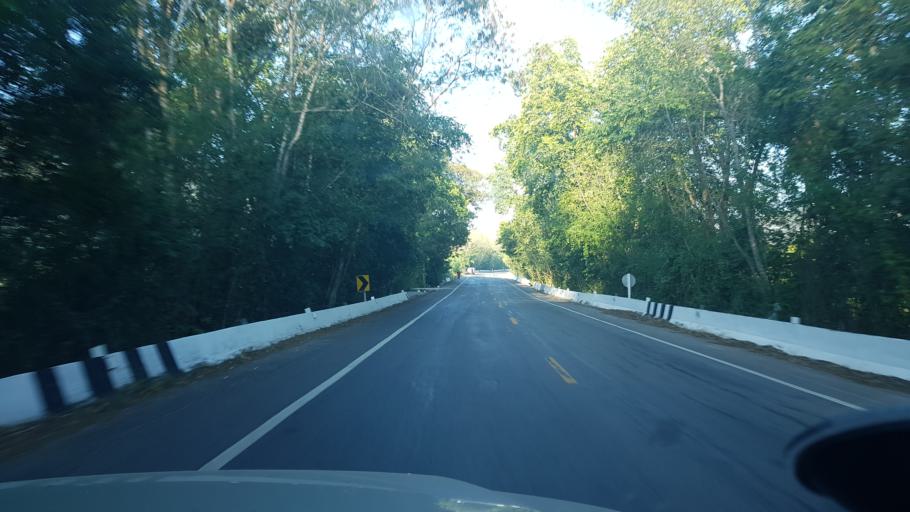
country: TH
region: Khon Kaen
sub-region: Amphoe Phu Pha Man
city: Phu Pha Man
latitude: 16.6470
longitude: 101.7820
